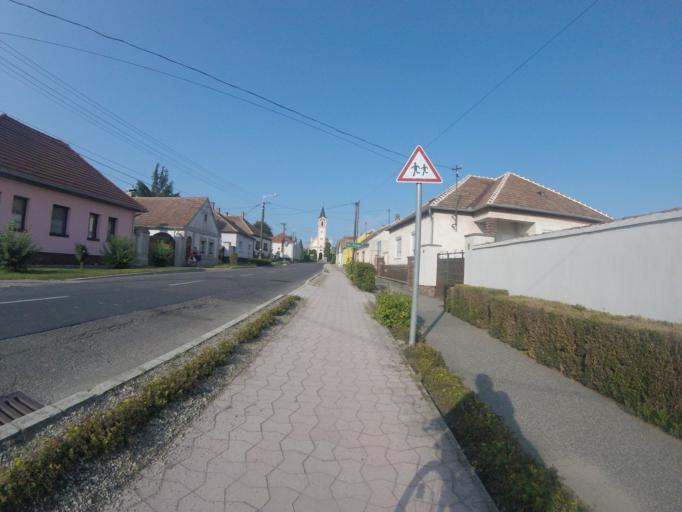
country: HU
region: Gyor-Moson-Sopron
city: Nagycenk
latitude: 47.6210
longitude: 16.7674
